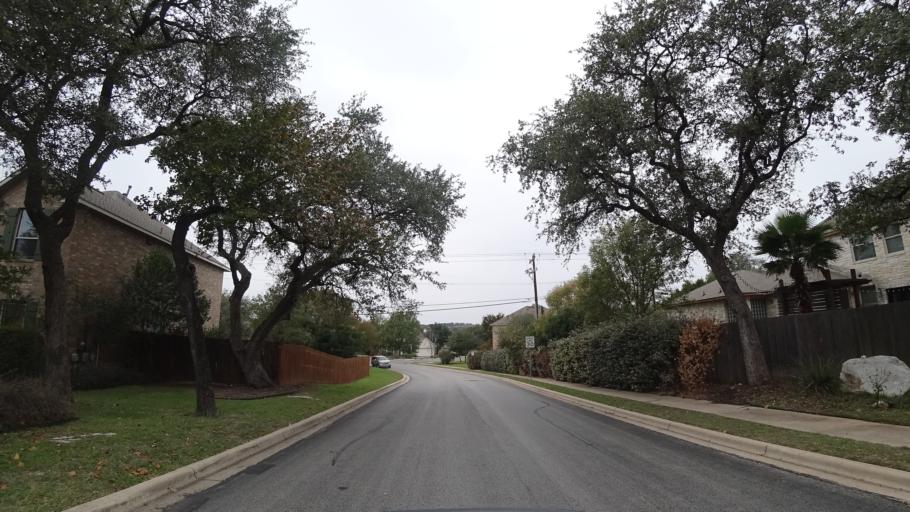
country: US
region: Texas
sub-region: Travis County
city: Shady Hollow
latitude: 30.1942
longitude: -97.8935
